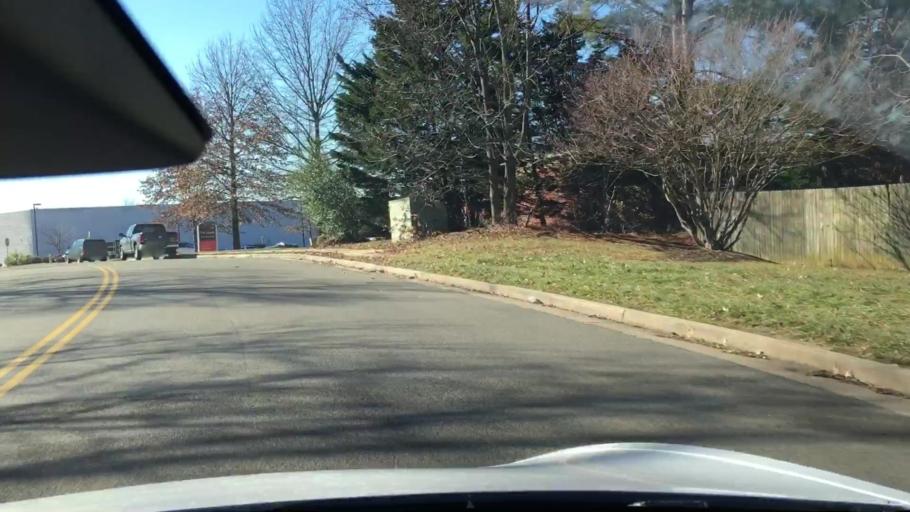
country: US
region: Virginia
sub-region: Henrico County
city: Short Pump
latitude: 37.6448
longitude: -77.5630
